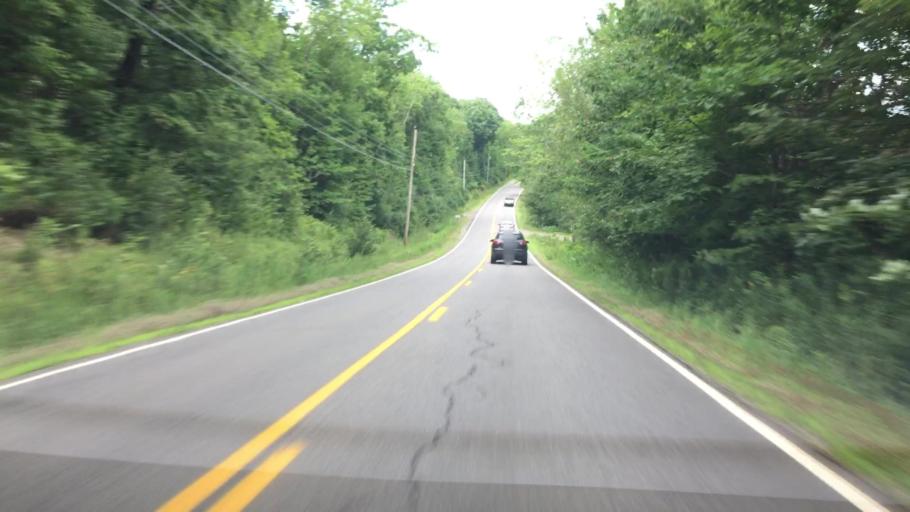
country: US
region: Maine
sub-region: Waldo County
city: Belfast
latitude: 44.3608
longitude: -69.0458
